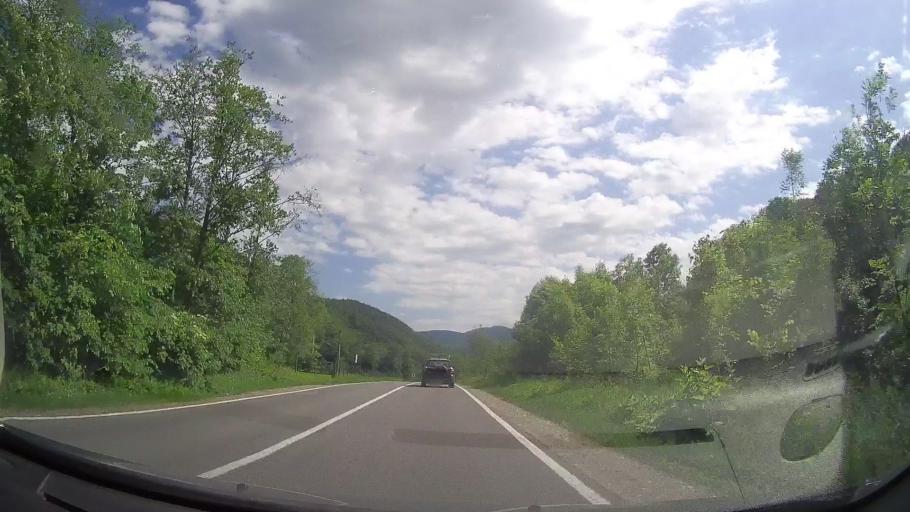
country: RO
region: Prahova
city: Maneciu
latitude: 45.3913
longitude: 25.9306
